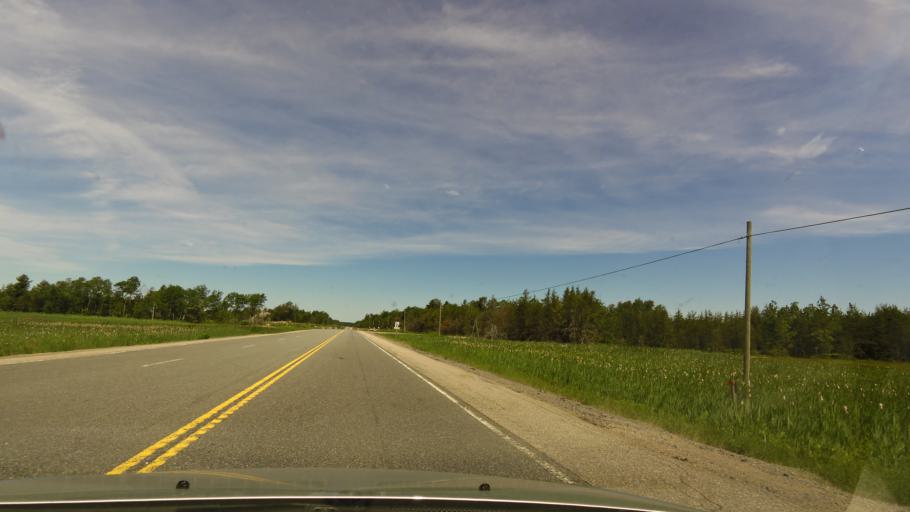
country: CA
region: Ontario
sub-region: Parry Sound District
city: Parry Sound
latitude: 45.4635
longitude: -80.1603
